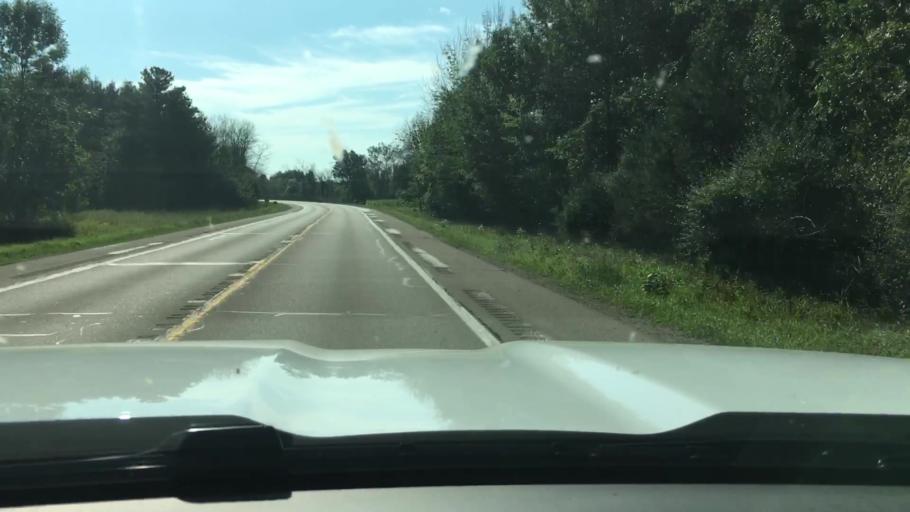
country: US
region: Michigan
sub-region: Montcalm County
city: Edmore
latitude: 43.4106
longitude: -85.1199
